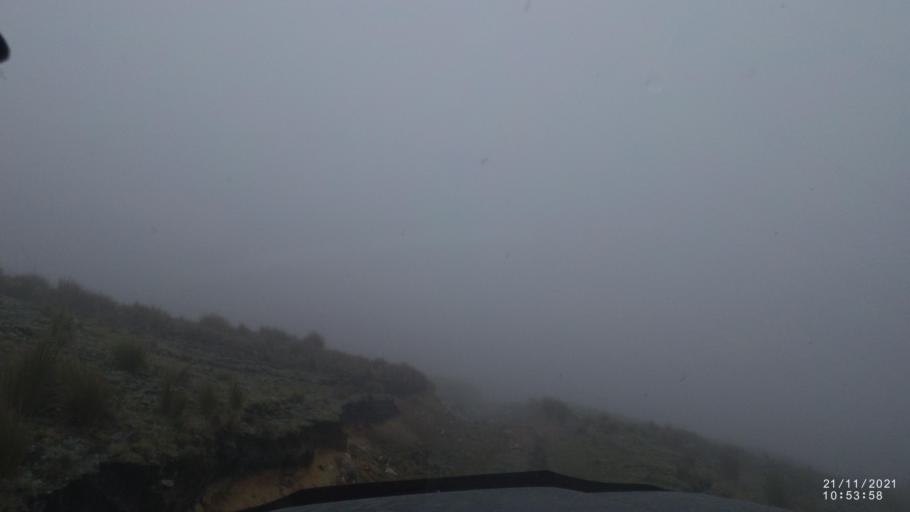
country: BO
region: Cochabamba
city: Cochabamba
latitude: -16.9664
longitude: -66.2706
